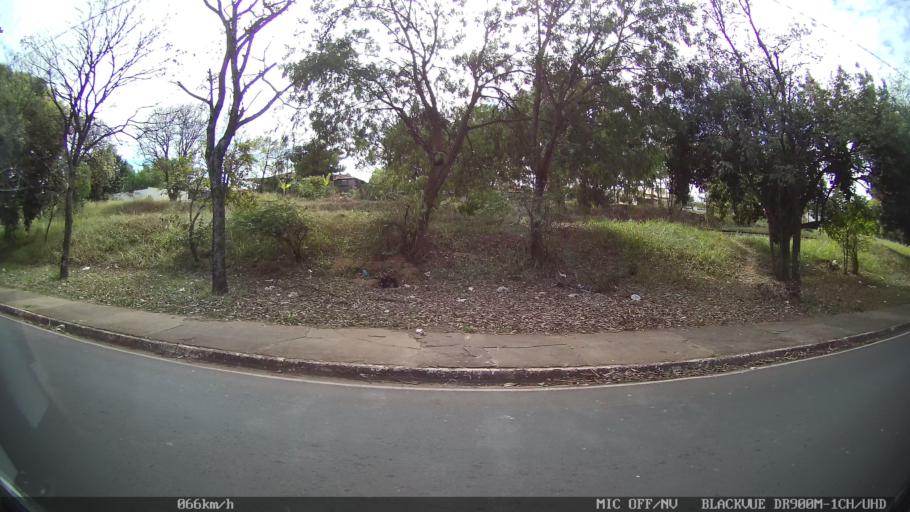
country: BR
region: Sao Paulo
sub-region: Catanduva
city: Catanduva
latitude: -21.1383
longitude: -48.9646
